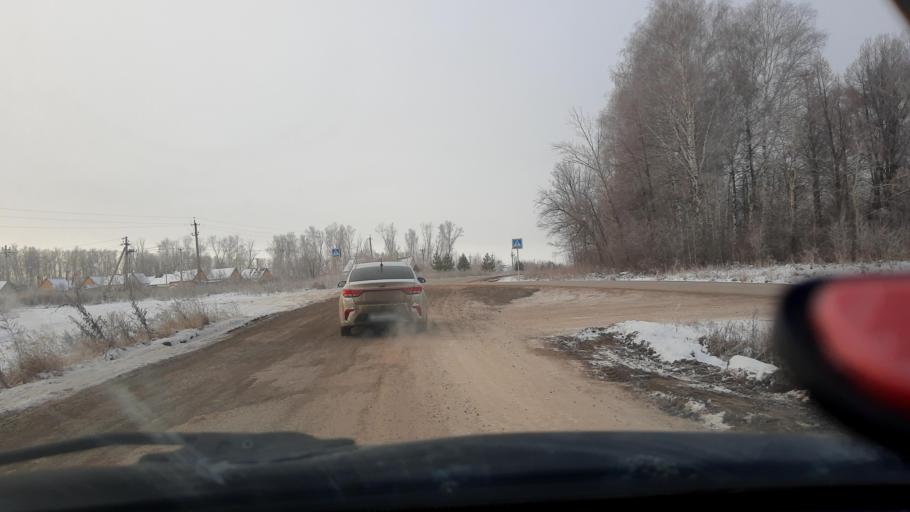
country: RU
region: Bashkortostan
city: Iglino
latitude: 54.8383
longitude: 56.4518
